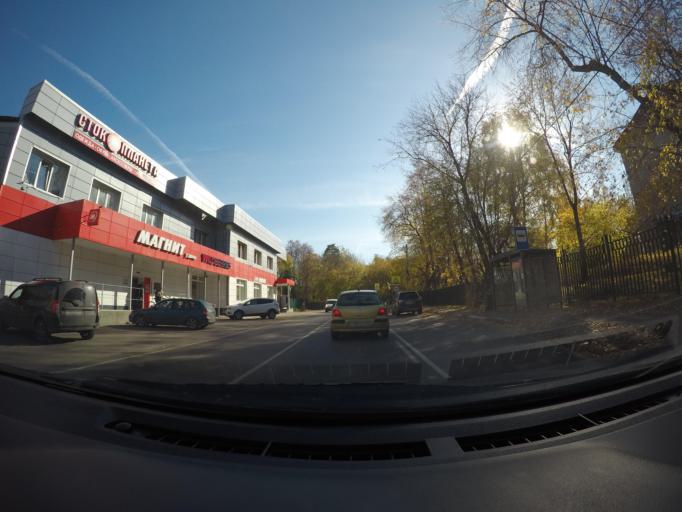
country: RU
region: Moskovskaya
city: Rodniki
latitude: 55.6395
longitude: 38.0539
